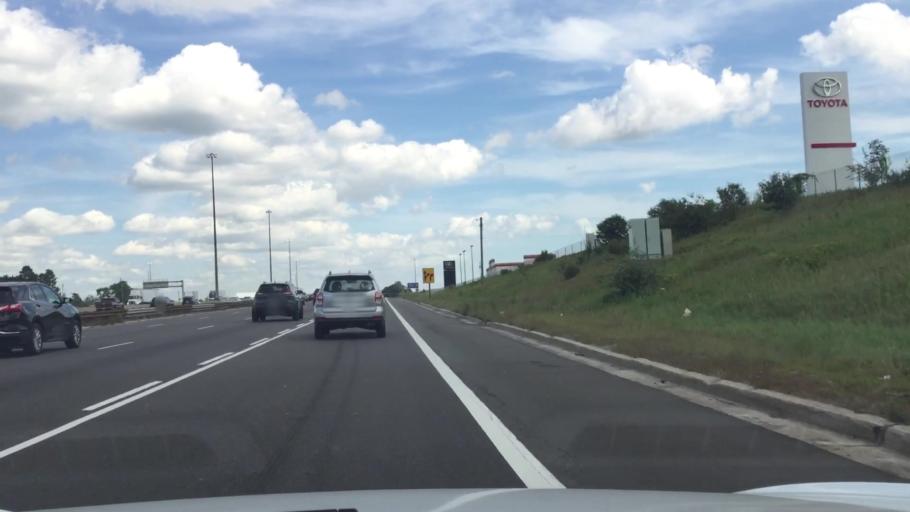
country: CA
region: Ontario
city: Scarborough
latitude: 43.7831
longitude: -79.2421
